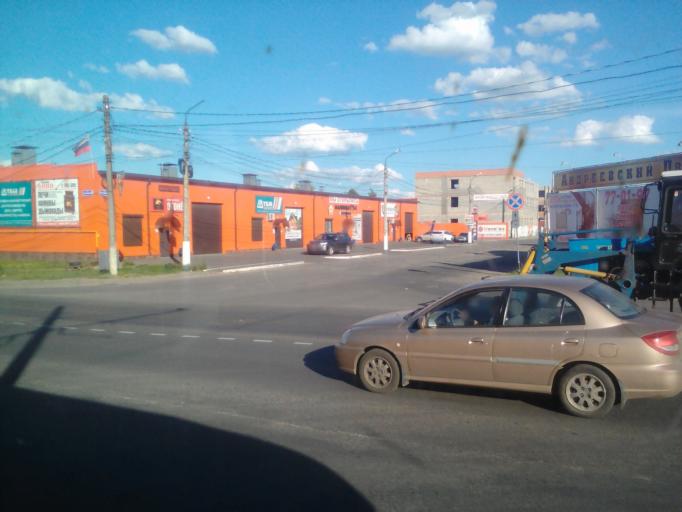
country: RU
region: Kursk
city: Kursk
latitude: 51.7069
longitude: 36.1769
